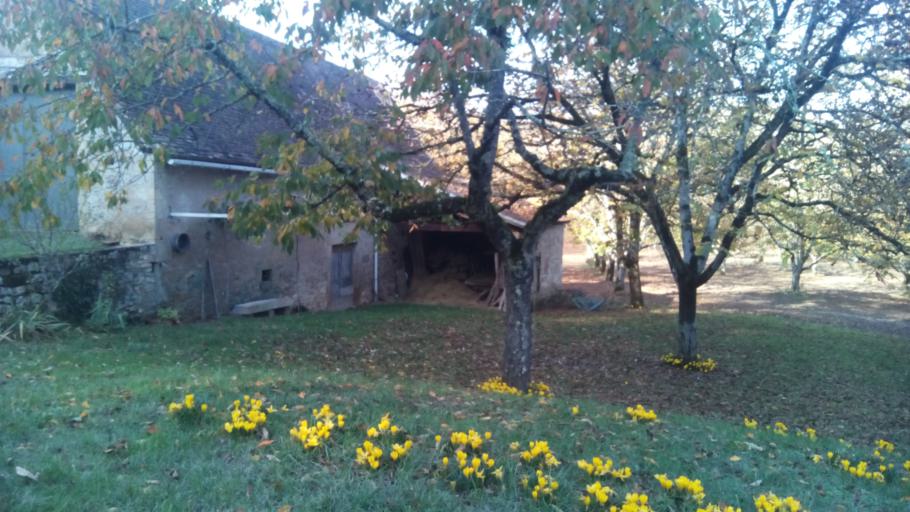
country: FR
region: Midi-Pyrenees
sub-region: Departement du Lot
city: Cajarc
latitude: 44.4728
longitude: 1.8286
